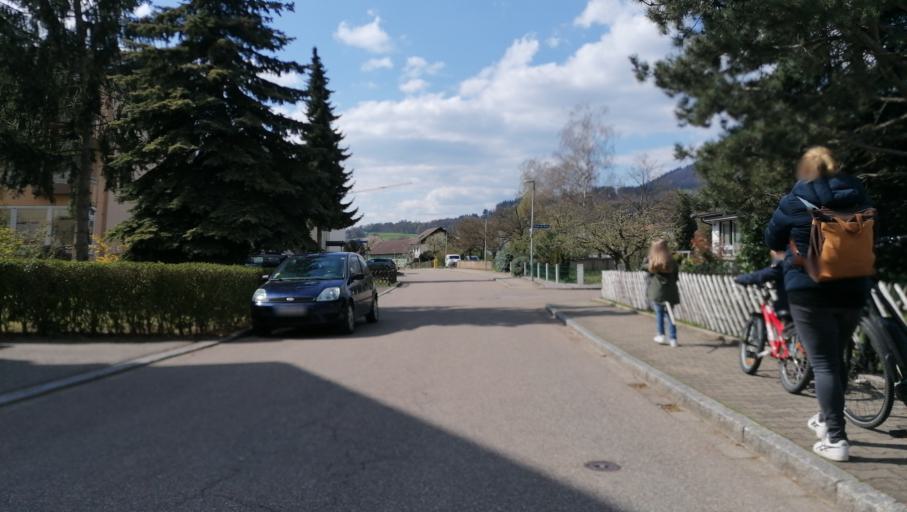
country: CH
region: Aargau
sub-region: Bezirk Rheinfelden
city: Stein
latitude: 47.5587
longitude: 7.9708
